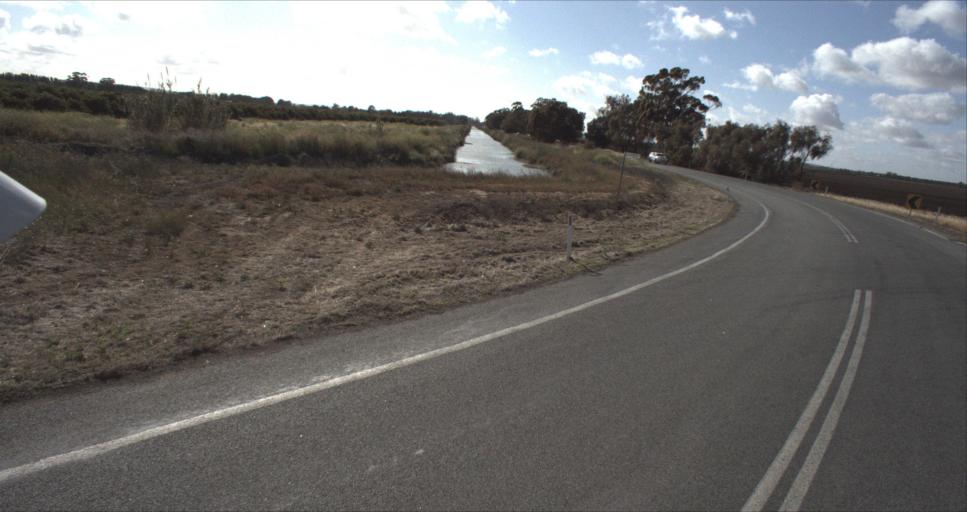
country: AU
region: New South Wales
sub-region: Leeton
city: Leeton
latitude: -34.5490
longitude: 146.3556
